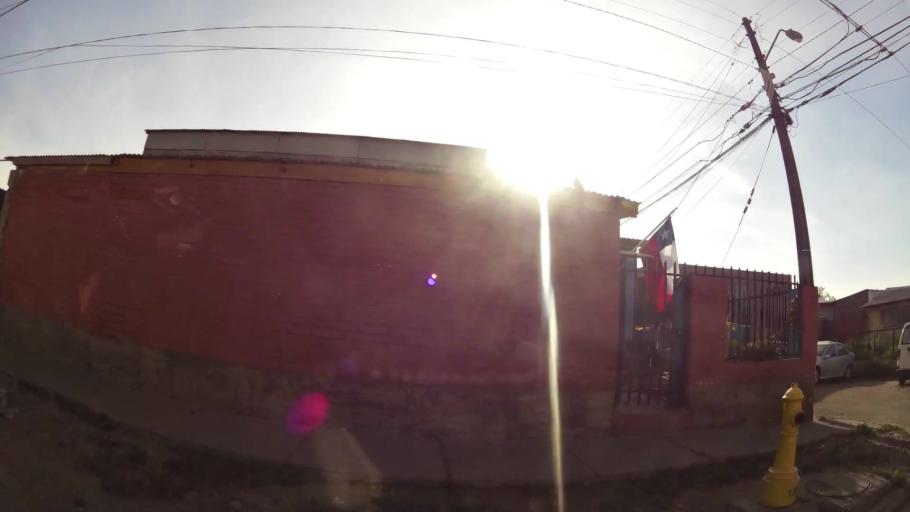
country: CL
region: Santiago Metropolitan
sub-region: Provincia de Santiago
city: La Pintana
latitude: -33.5453
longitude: -70.5840
